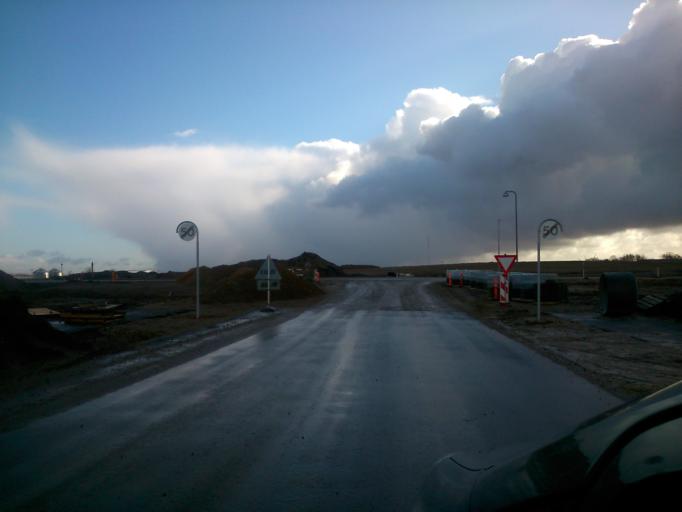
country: DK
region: Central Jutland
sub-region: Holstebro Kommune
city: Holstebro
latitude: 56.3909
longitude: 8.6225
